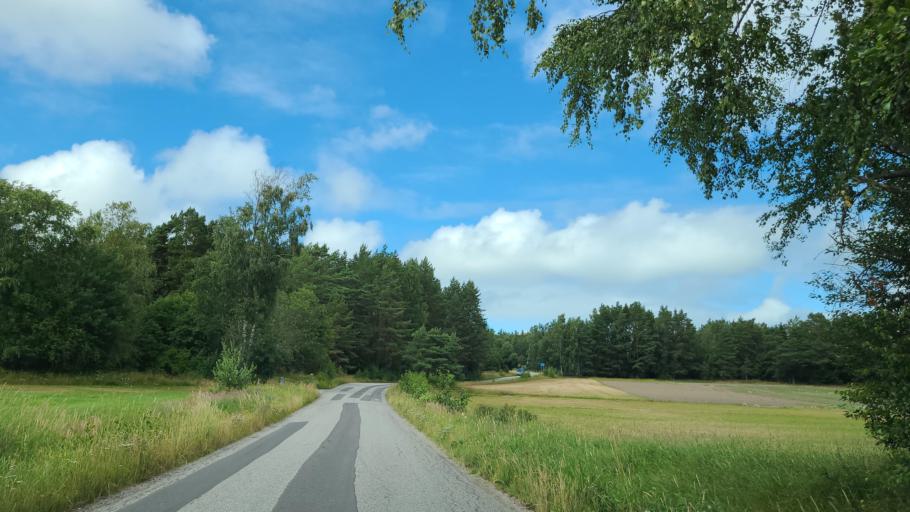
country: FI
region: Varsinais-Suomi
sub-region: Aboland-Turunmaa
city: Nagu
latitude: 60.1784
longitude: 21.9742
